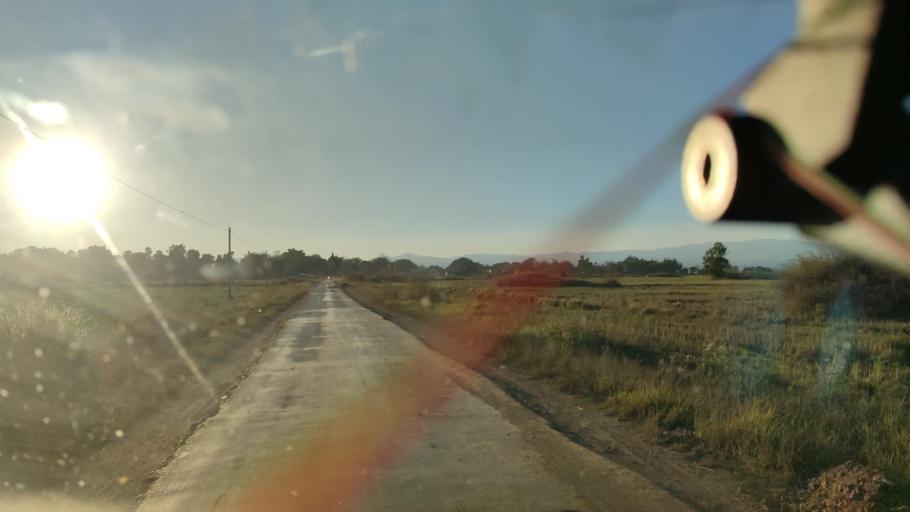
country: MM
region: Shan
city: Taunggyi
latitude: 20.4602
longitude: 97.2056
